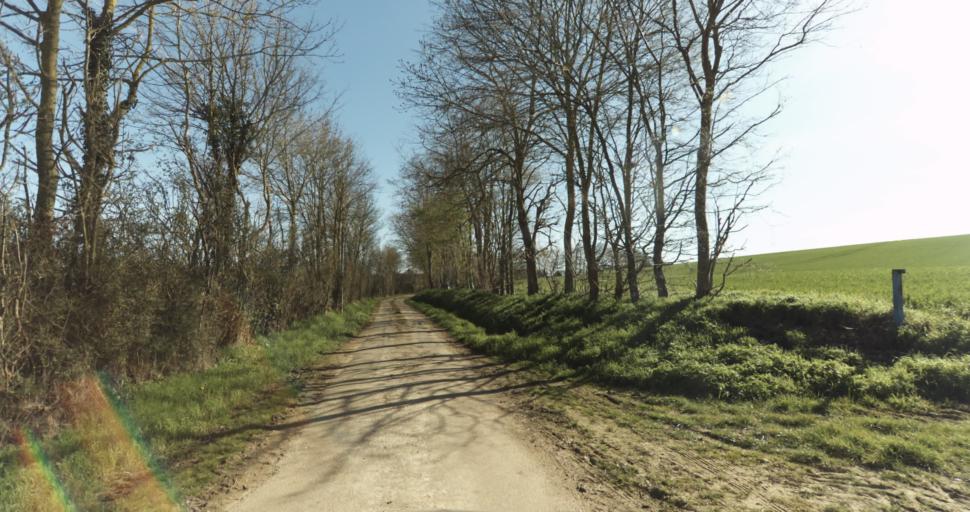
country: FR
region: Lower Normandy
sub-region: Departement du Calvados
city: Saint-Pierre-sur-Dives
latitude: 49.0200
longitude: 0.0142
